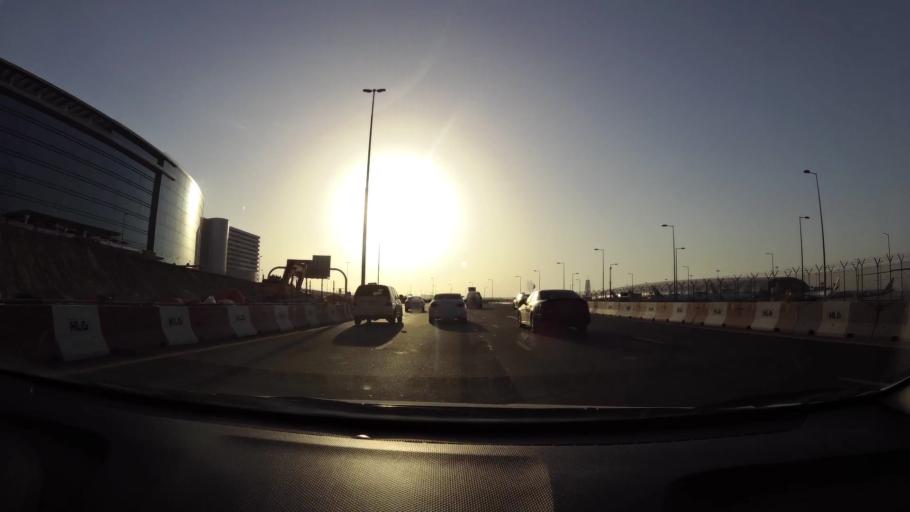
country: AE
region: Ash Shariqah
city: Sharjah
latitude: 25.2423
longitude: 55.3672
